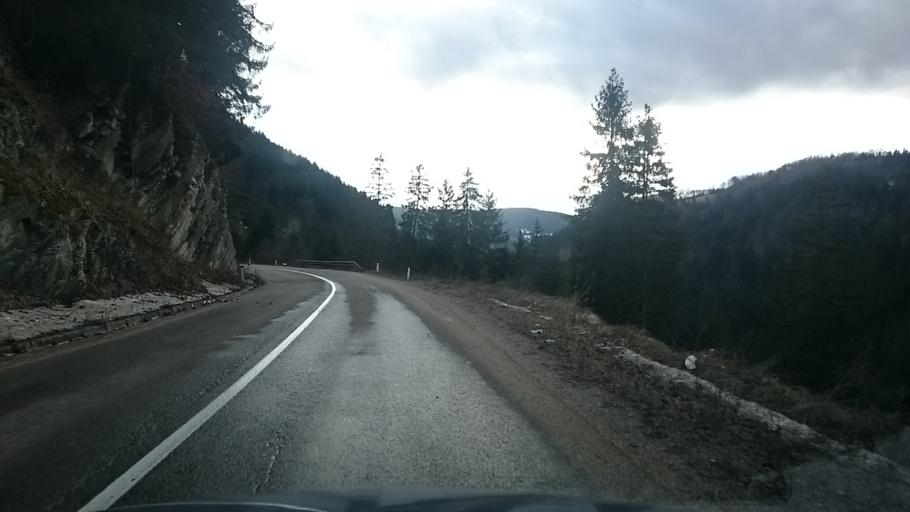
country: BA
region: Republika Srpska
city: Skender Vakuf
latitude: 44.4713
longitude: 17.3790
